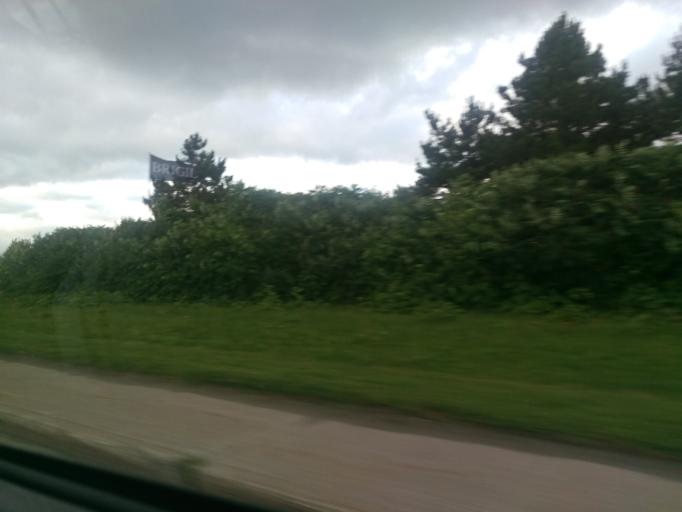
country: CA
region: Quebec
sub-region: Outaouais
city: Gatineau
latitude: 45.4760
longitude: -75.7430
